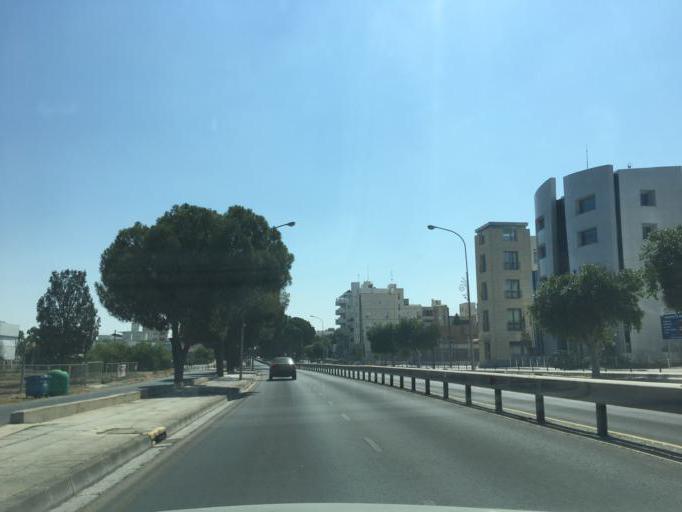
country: CY
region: Lefkosia
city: Nicosia
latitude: 35.1645
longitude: 33.3226
